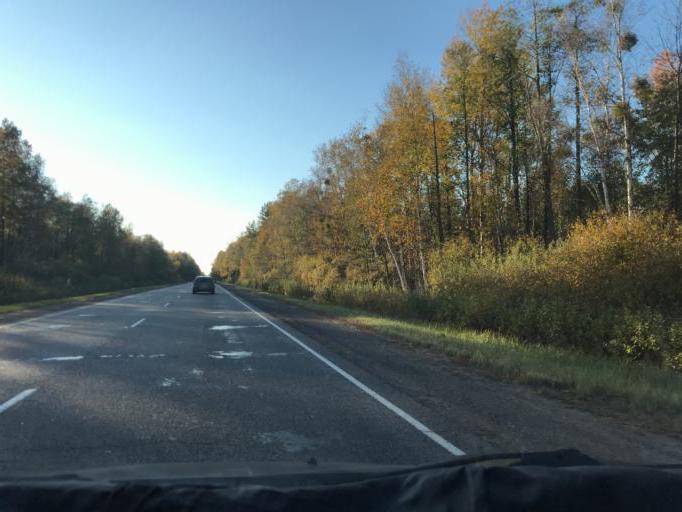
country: BY
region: Gomel
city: Zhytkavichy
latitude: 52.2746
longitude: 28.1688
